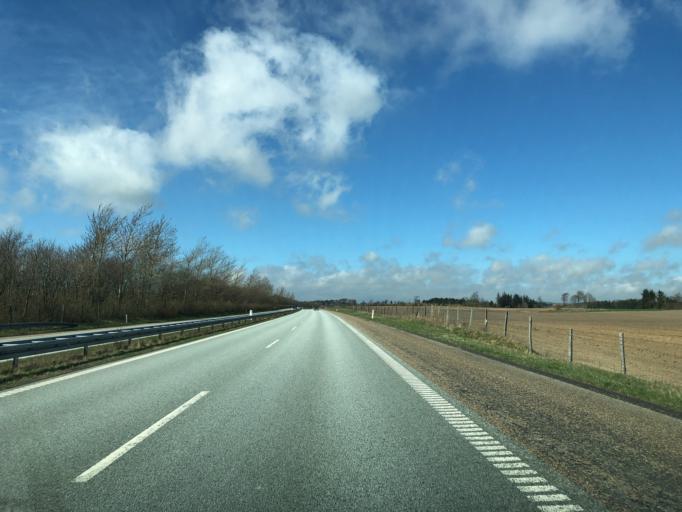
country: DK
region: North Denmark
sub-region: Hjorring Kommune
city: Hjorring
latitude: 57.4893
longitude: 10.0255
